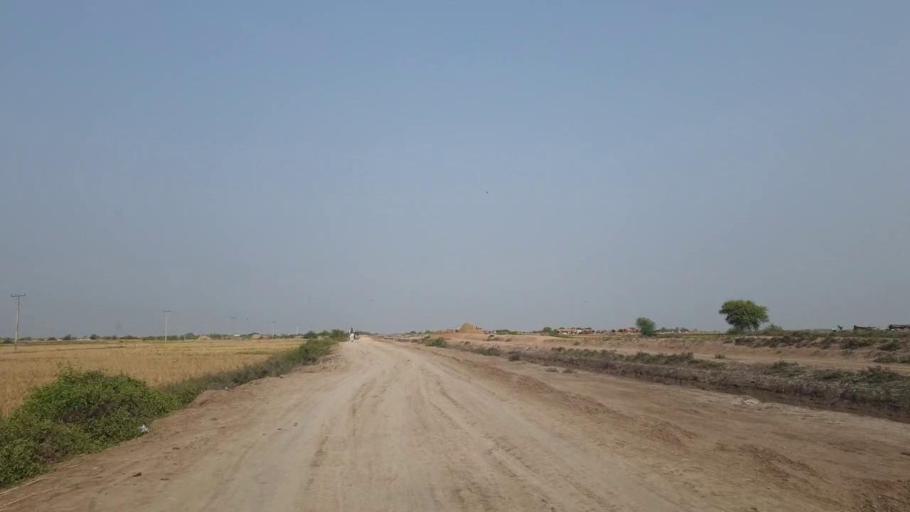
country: PK
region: Sindh
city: Badin
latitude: 24.7088
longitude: 68.7740
